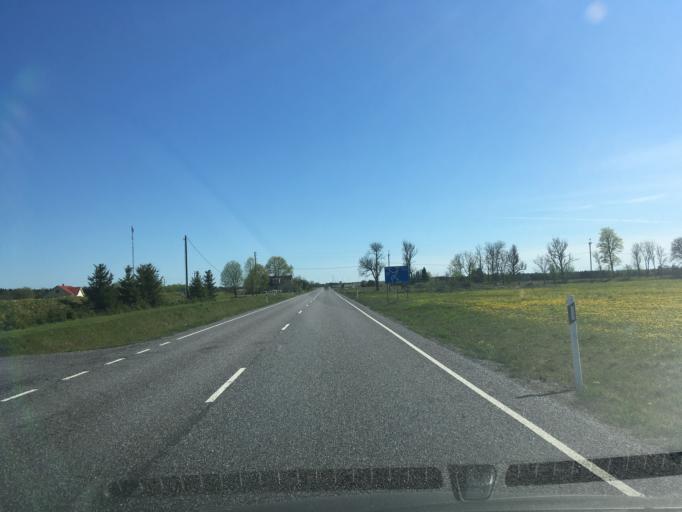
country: EE
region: Harju
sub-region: Rae vald
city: Vaida
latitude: 59.2578
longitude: 25.0177
